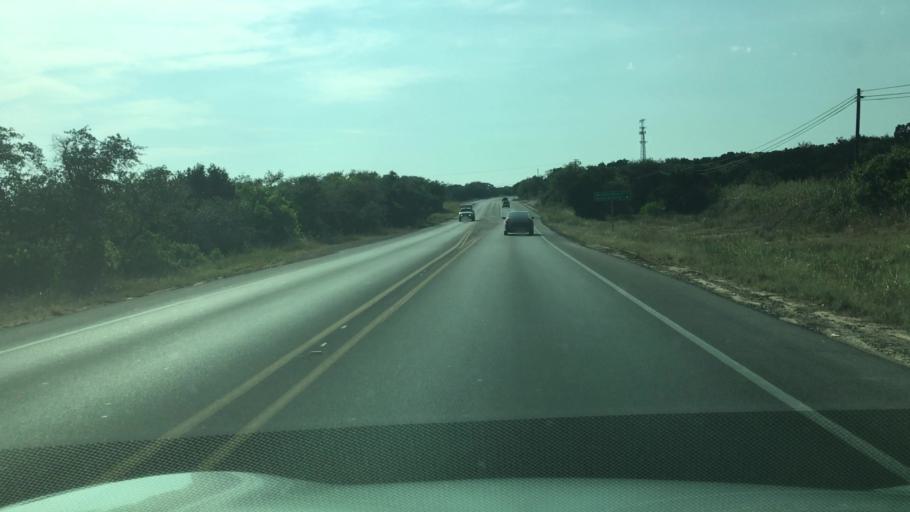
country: US
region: Texas
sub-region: Hays County
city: Wimberley
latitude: 29.9187
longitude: -98.0546
